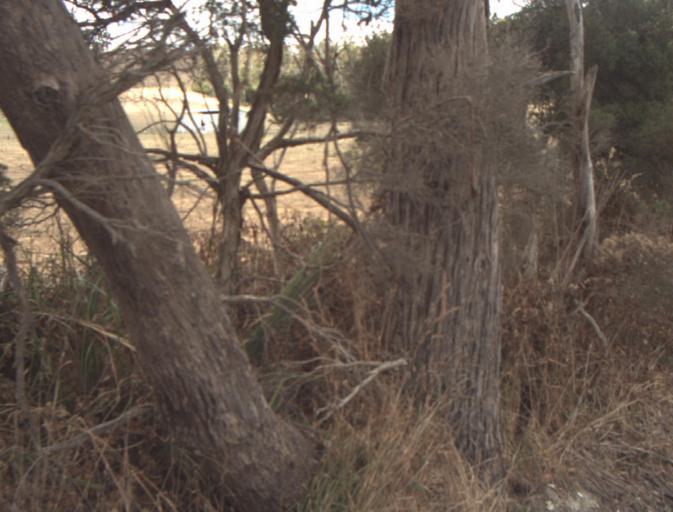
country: AU
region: Tasmania
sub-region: Launceston
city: Mayfield
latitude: -41.2417
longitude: 147.1650
